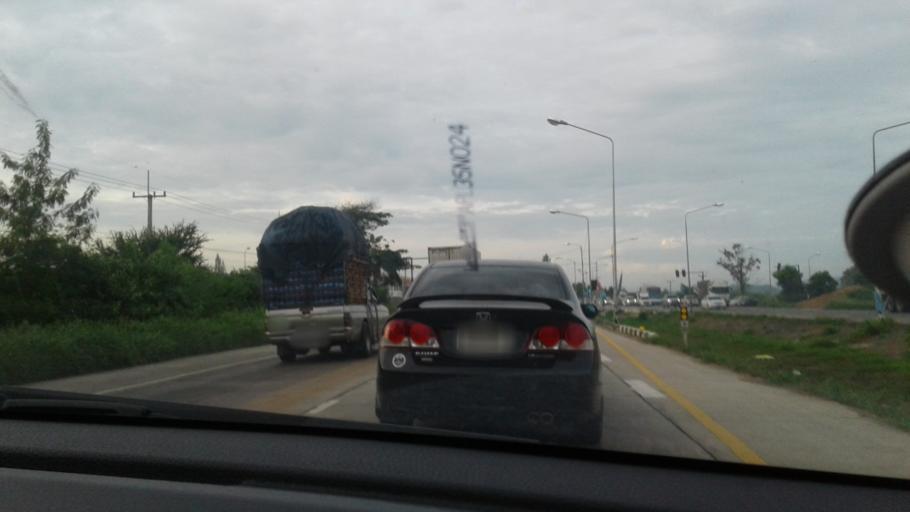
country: TH
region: Prachuap Khiri Khan
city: Pran Buri
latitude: 12.4838
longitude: 99.8916
